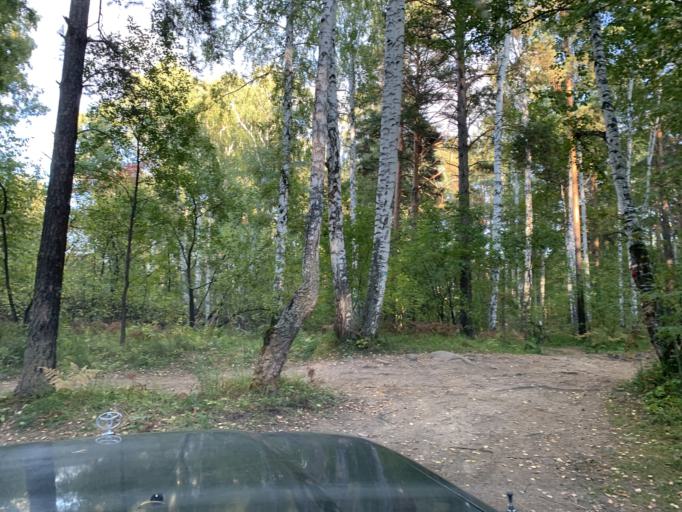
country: RU
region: Chelyabinsk
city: Vishnevogorsk
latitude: 56.0022
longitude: 60.5107
